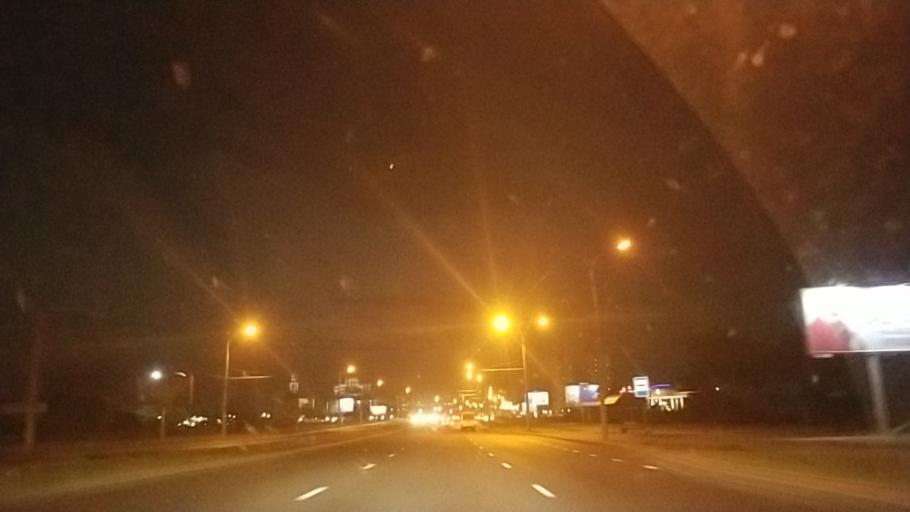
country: BY
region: Brest
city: Brest
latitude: 52.0934
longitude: 23.7678
